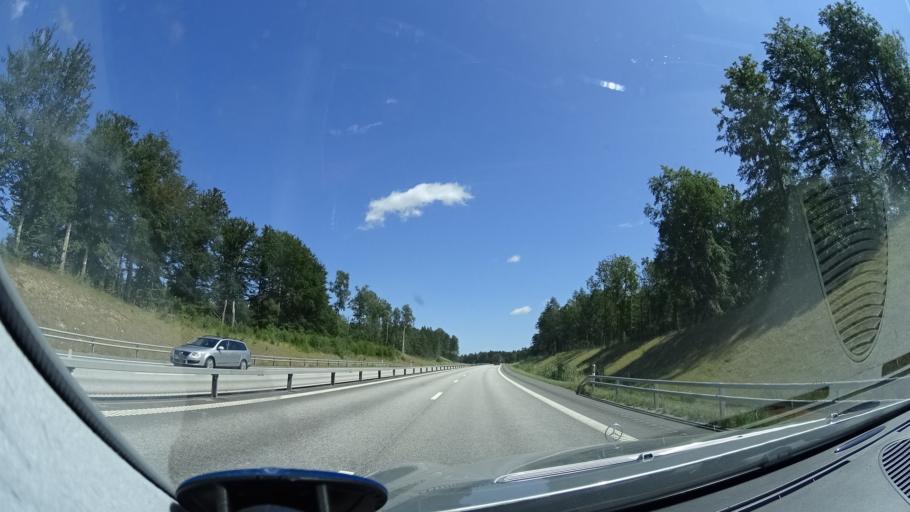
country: SE
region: Skane
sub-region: Horby Kommun
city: Hoerby
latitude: 55.9035
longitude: 13.7325
